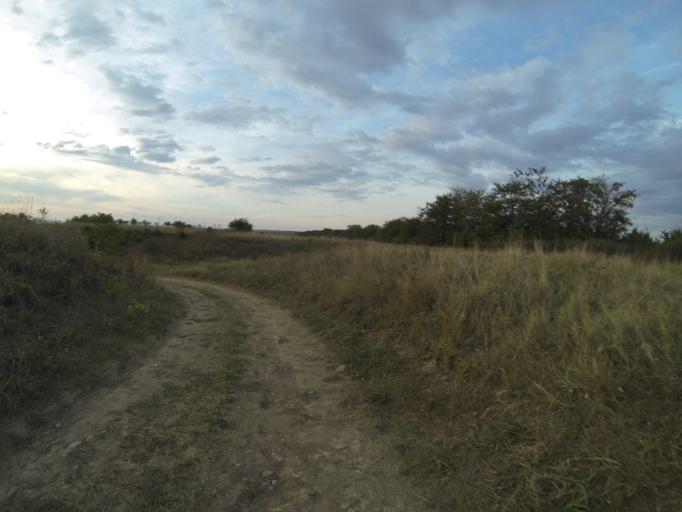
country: RO
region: Dolj
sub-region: Comuna Ceratu
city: Ceratu
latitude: 44.0869
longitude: 23.6750
